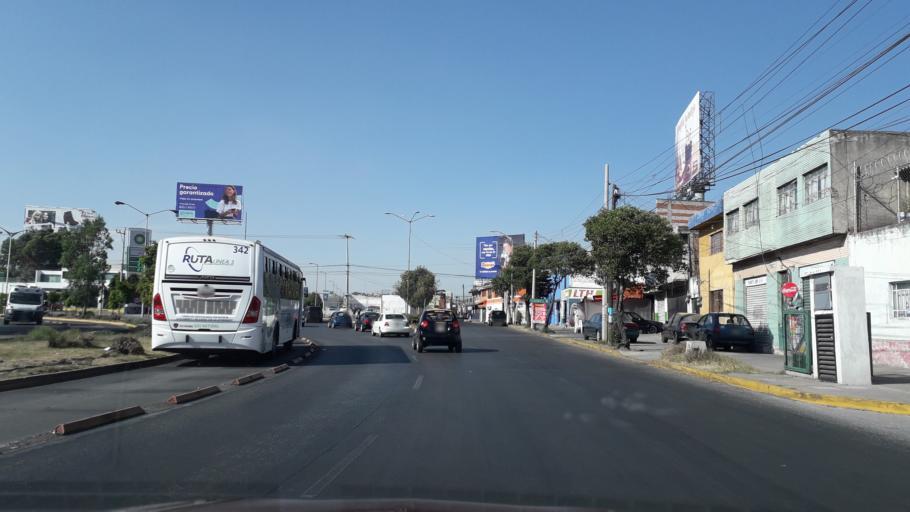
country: MX
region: Puebla
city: Puebla
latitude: 19.0698
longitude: -98.1914
